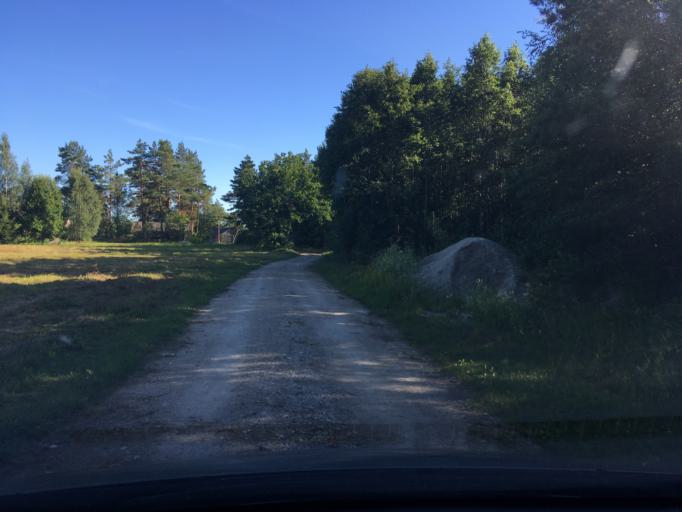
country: EE
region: Laeaene
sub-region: Lihula vald
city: Lihula
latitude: 58.5850
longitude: 23.7361
